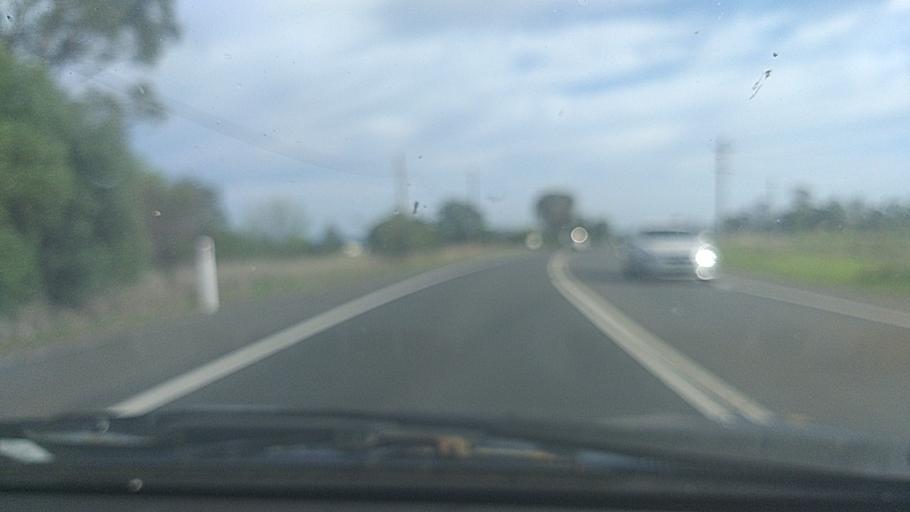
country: AU
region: New South Wales
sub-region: Liverpool
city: Luddenham
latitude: -33.8904
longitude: 150.6990
